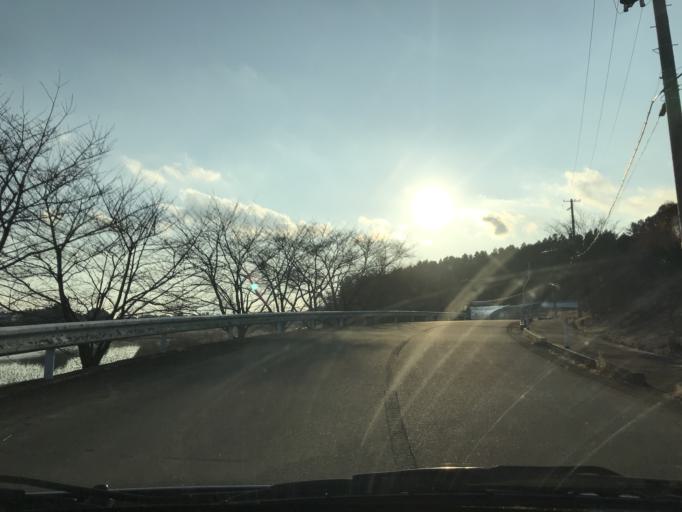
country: JP
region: Miyagi
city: Wakuya
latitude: 38.6830
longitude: 141.1129
